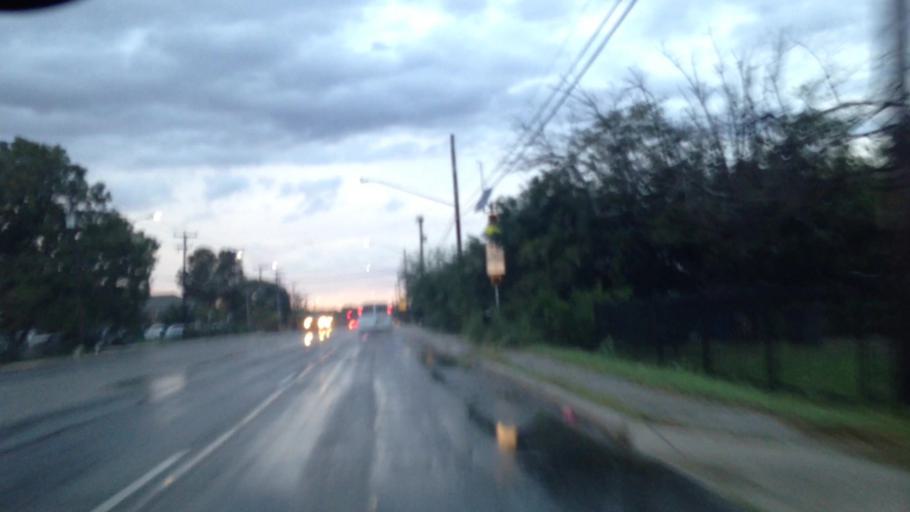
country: US
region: Texas
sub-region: Bexar County
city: Live Oak
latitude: 29.5731
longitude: -98.3692
